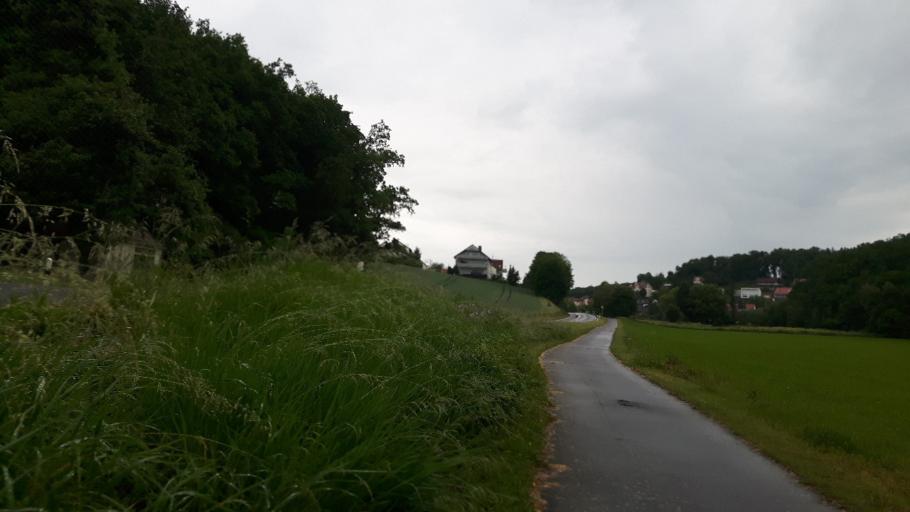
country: DE
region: Bavaria
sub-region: Regierungsbezirk Unterfranken
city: Uchtelhausen
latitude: 50.0884
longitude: 10.2468
